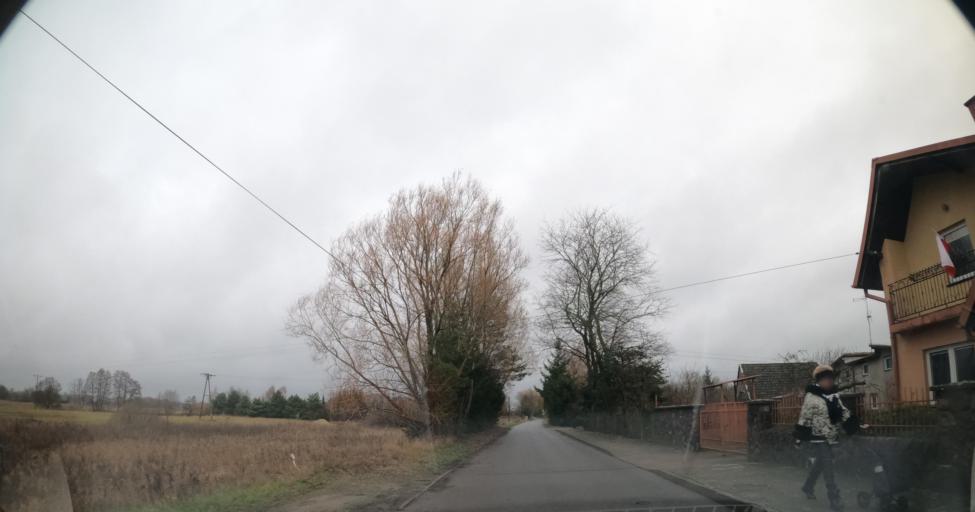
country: PL
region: West Pomeranian Voivodeship
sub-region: Powiat drawski
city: Drawsko Pomorskie
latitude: 53.5332
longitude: 15.8236
